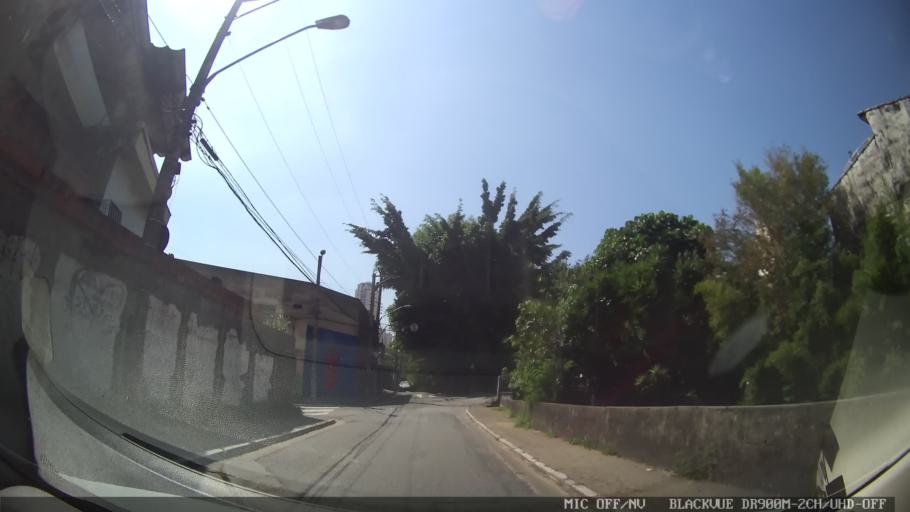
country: BR
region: Sao Paulo
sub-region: Sao Paulo
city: Sao Paulo
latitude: -23.4844
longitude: -46.6341
